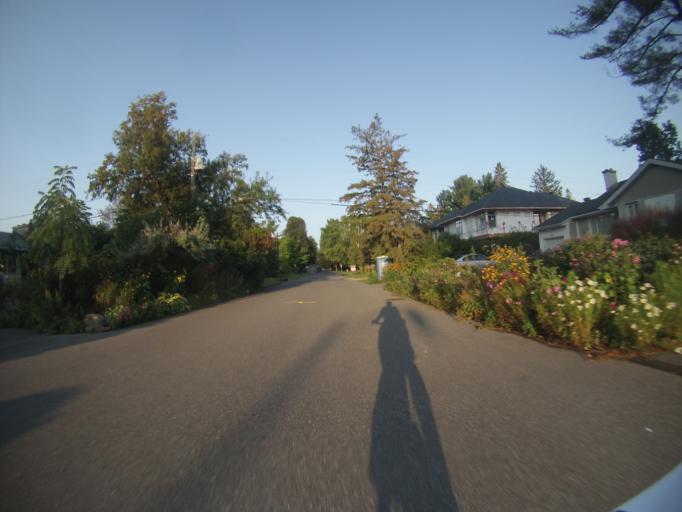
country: CA
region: Ontario
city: Ottawa
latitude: 45.3965
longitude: -75.6557
